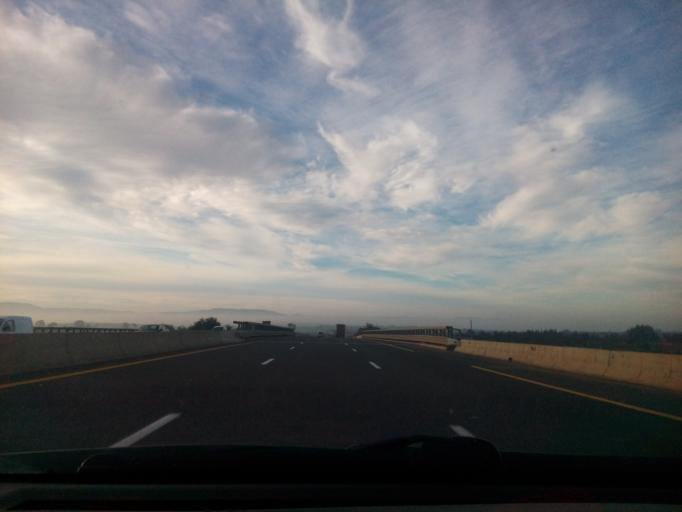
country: DZ
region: Relizane
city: Relizane
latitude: 35.7234
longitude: 0.3009
